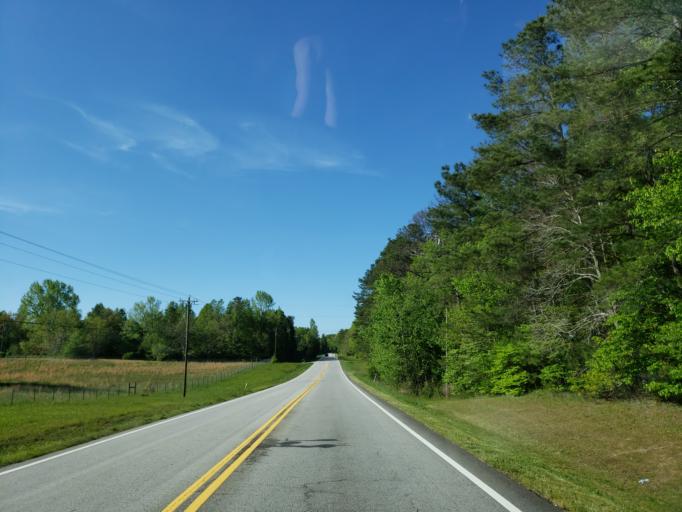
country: US
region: Georgia
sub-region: Haralson County
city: Tallapoosa
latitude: 33.8881
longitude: -85.3117
